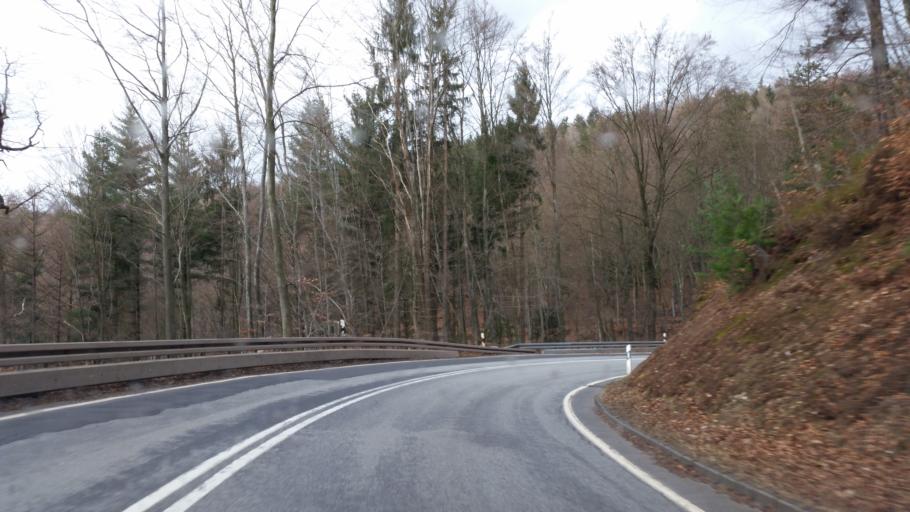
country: DE
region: Bavaria
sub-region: Regierungsbezirk Unterfranken
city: Heigenbrucken
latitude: 49.9980
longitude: 9.3507
